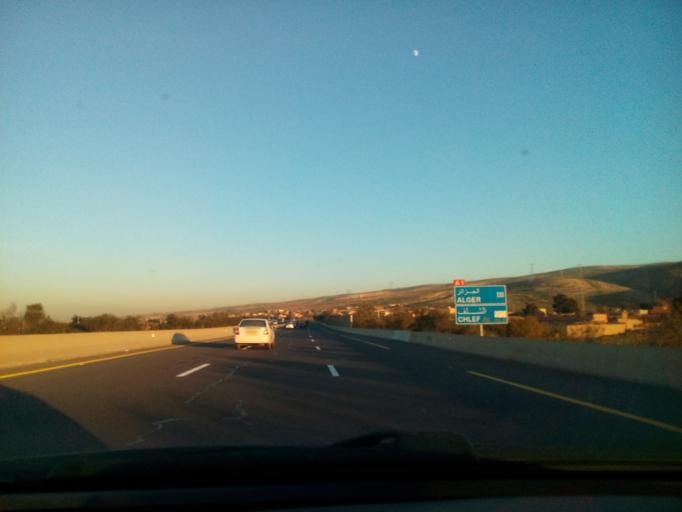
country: DZ
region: Chlef
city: Boukadir
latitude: 36.0265
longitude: 1.0613
